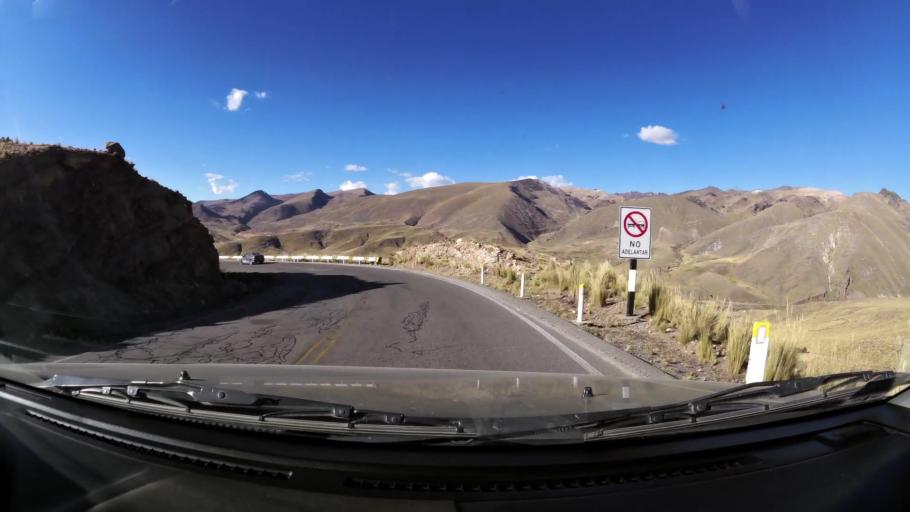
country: PE
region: Huancavelica
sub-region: Huaytara
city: Pilpichaca
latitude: -13.3703
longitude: -74.9543
